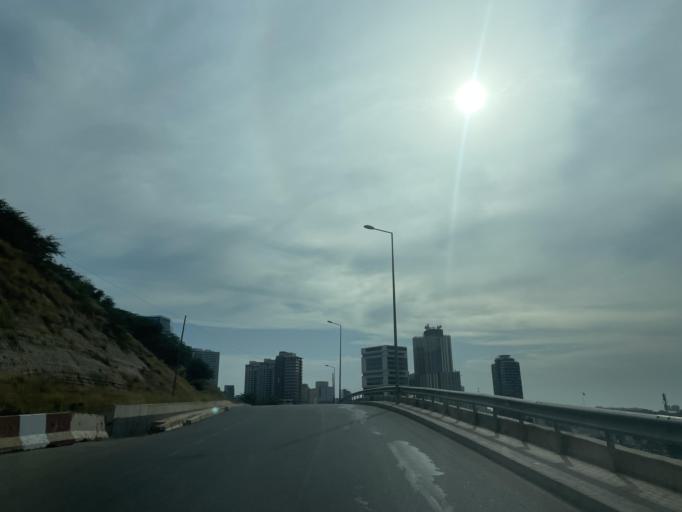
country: AO
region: Luanda
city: Luanda
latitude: -8.8069
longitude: 13.2468
